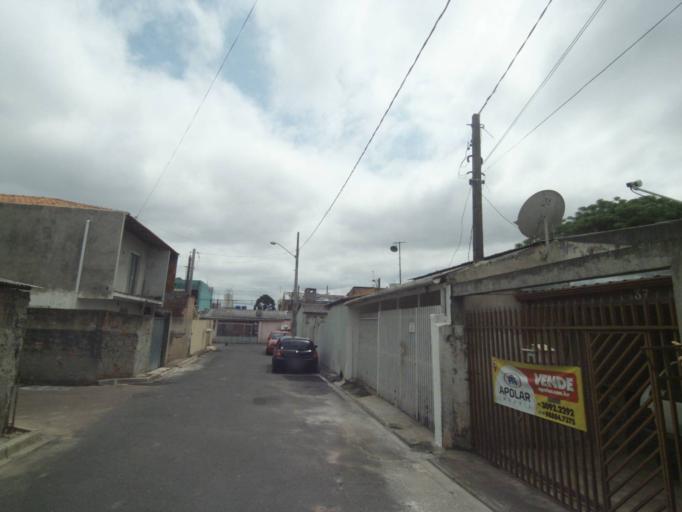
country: BR
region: Parana
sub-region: Sao Jose Dos Pinhais
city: Sao Jose dos Pinhais
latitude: -25.5354
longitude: -49.2667
